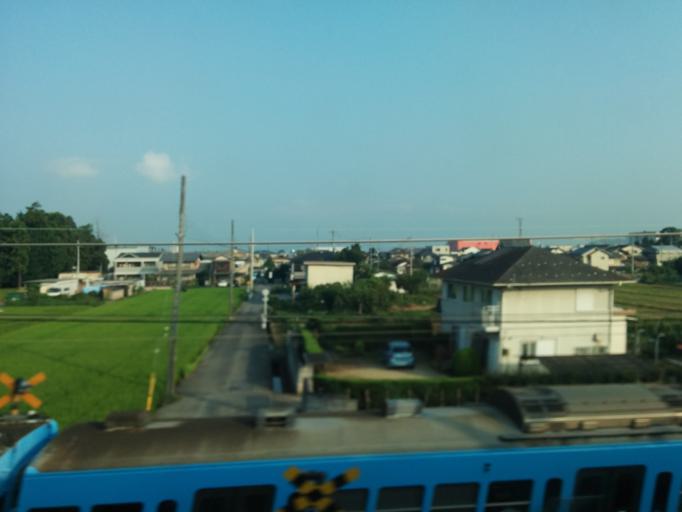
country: JP
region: Shiga Prefecture
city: Youkaichi
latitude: 35.1821
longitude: 136.2185
